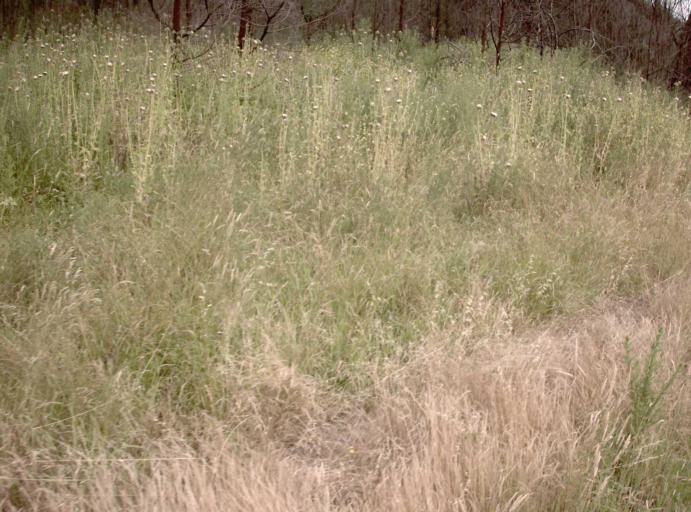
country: AU
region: Victoria
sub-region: Wellington
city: Heyfield
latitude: -37.7794
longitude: 146.6668
